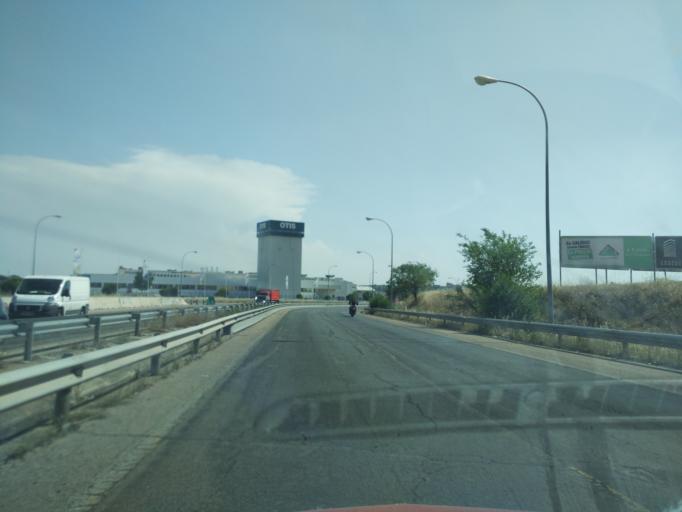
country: ES
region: Madrid
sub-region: Provincia de Madrid
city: Latina
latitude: 40.3581
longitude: -3.7476
